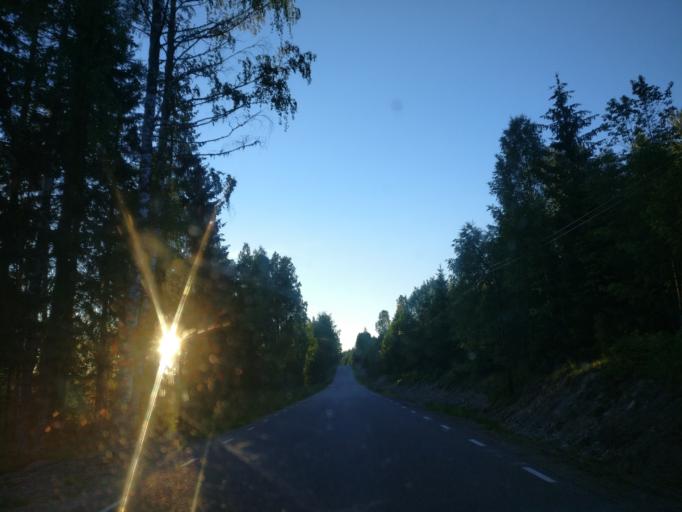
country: SE
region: Vaesternorrland
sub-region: Sundsvalls Kommun
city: Vi
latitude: 62.2422
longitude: 17.1177
